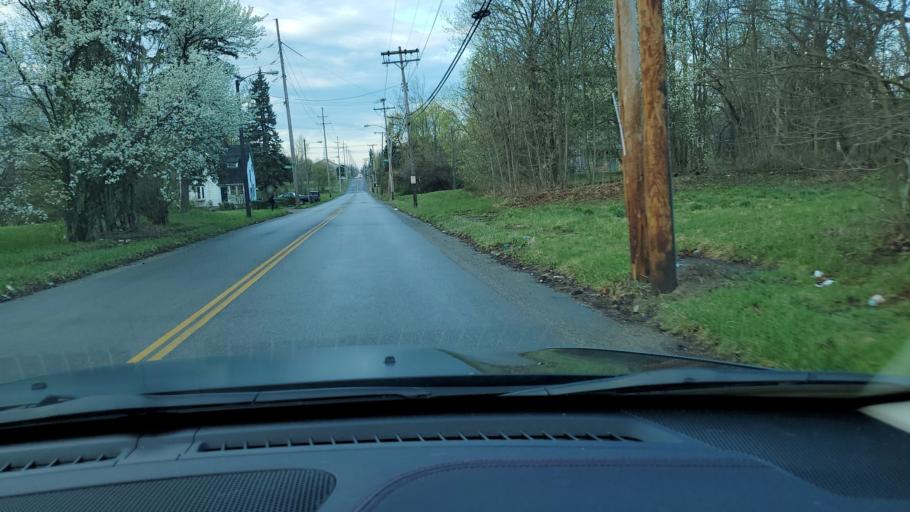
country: US
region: Ohio
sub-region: Mahoning County
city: Youngstown
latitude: 41.0911
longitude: -80.6640
